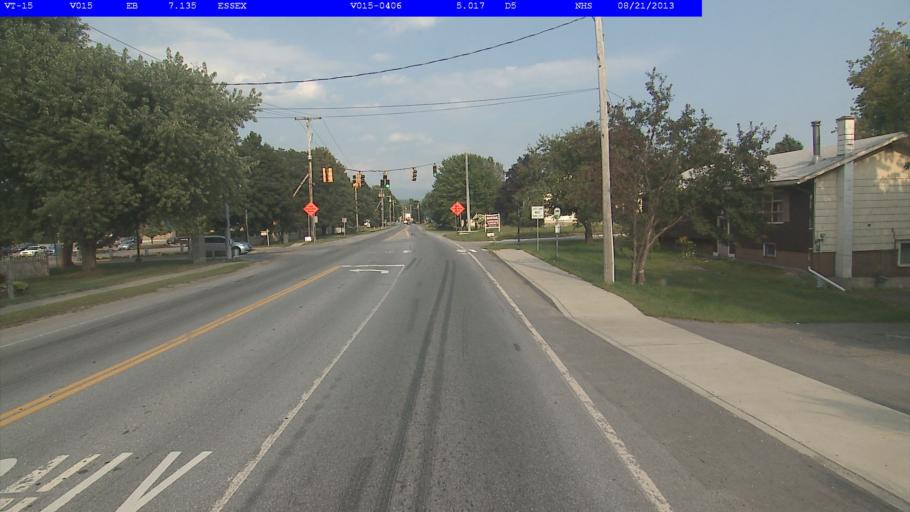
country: US
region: Vermont
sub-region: Chittenden County
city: Essex Junction
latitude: 44.5108
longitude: -73.0662
